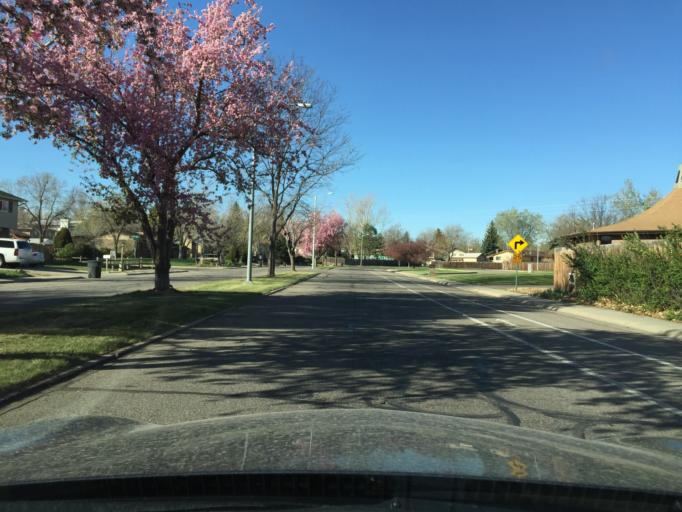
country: US
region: Colorado
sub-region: Boulder County
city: Longmont
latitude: 40.1402
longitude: -105.1080
